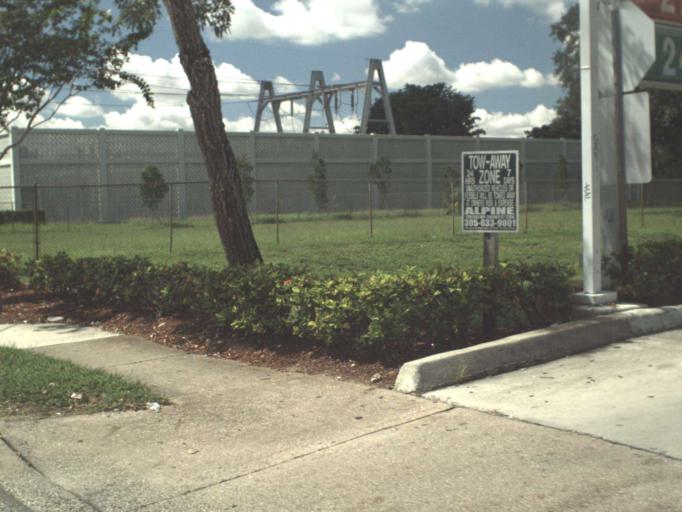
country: US
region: Florida
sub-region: Miami-Dade County
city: Golden Glades
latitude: 25.9144
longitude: -80.2119
